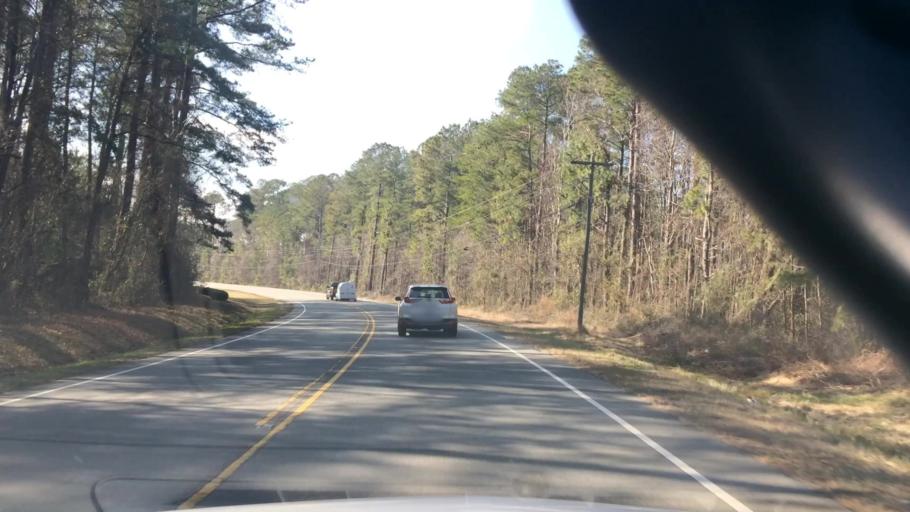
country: US
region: North Carolina
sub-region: Duplin County
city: Wallace
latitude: 34.7635
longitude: -77.9425
